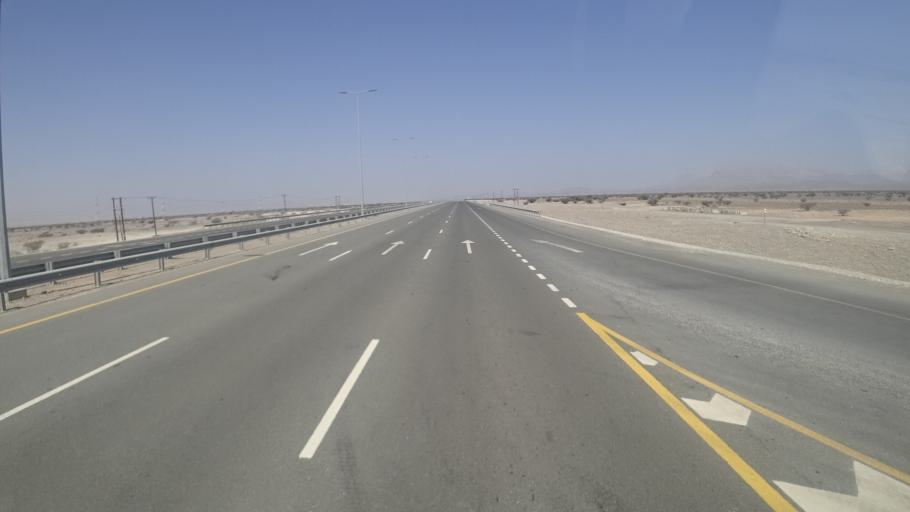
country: OM
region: Ash Sharqiyah
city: Badiyah
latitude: 22.3635
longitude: 59.1098
